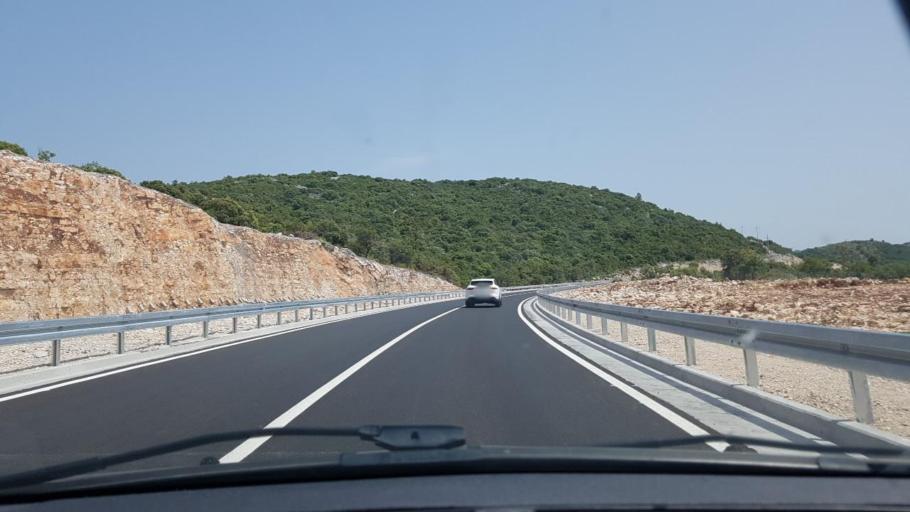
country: HR
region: Dubrovacko-Neretvanska
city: Ston
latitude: 42.9520
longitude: 17.7562
